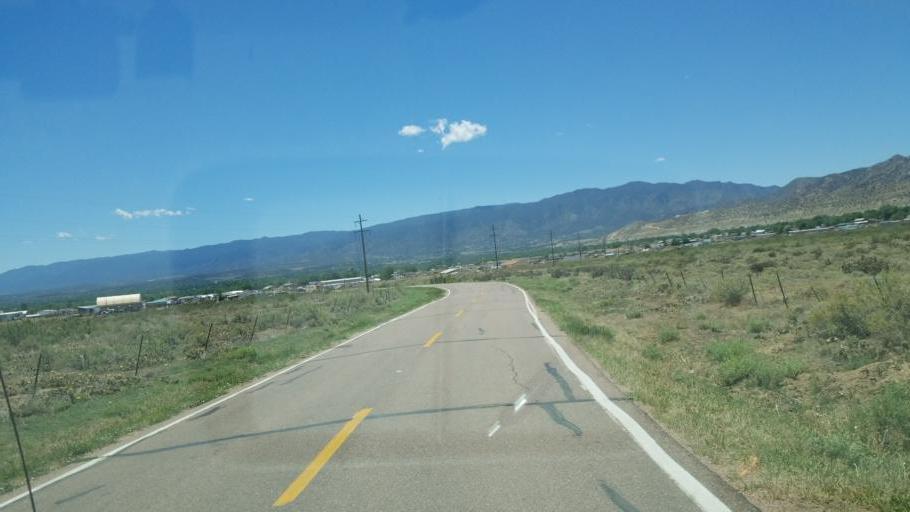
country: US
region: Colorado
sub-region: Fremont County
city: Canon City
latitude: 38.4788
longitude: -105.2221
